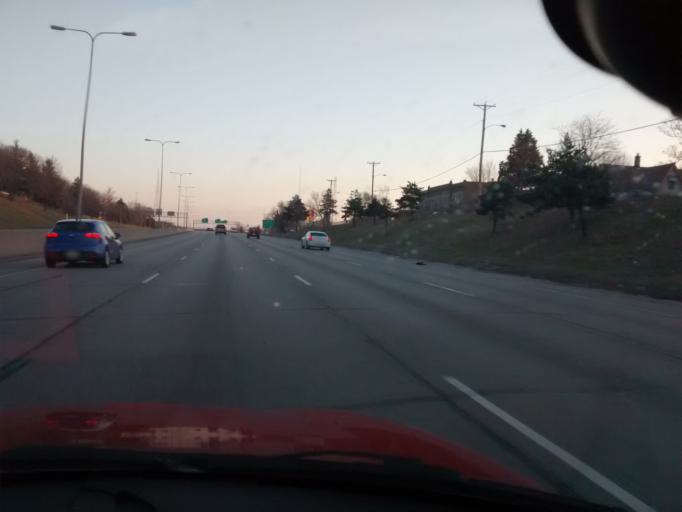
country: US
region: Nebraska
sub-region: Douglas County
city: Omaha
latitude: 41.2454
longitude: -95.9535
